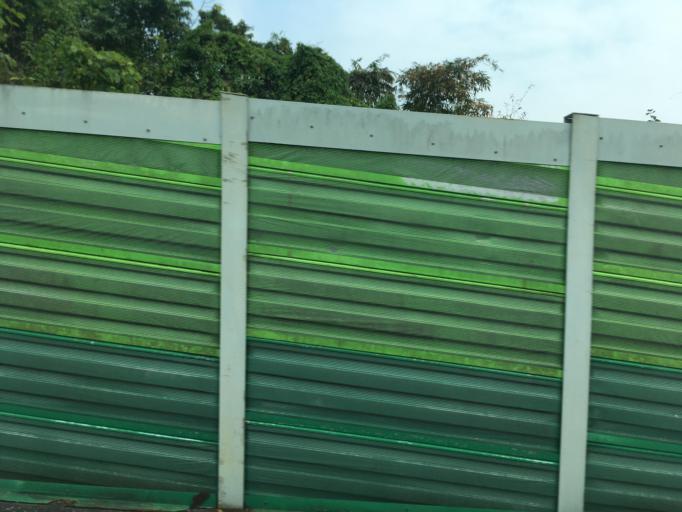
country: TW
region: Taipei
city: Taipei
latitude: 25.0225
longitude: 121.6343
